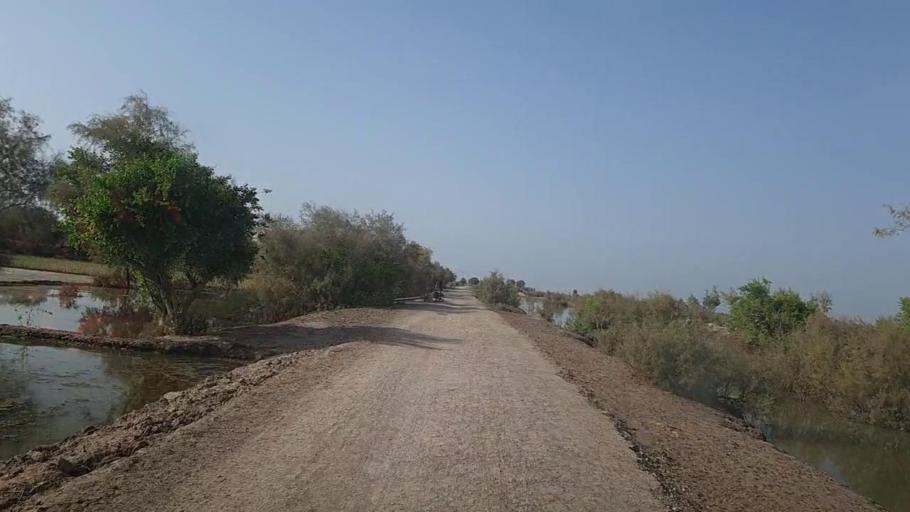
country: PK
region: Sindh
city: Sita Road
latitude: 27.1009
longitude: 67.8738
